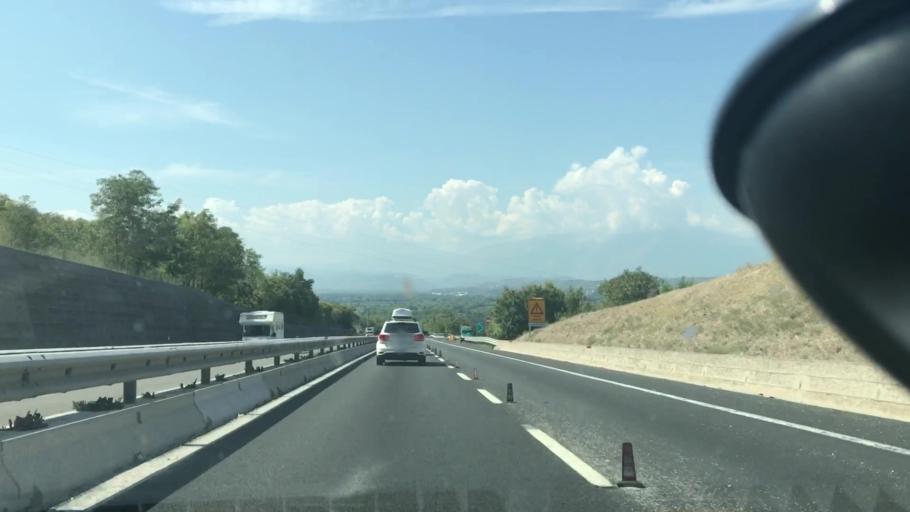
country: IT
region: Abruzzo
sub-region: Provincia di Chieti
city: Torino di Sangro
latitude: 42.2027
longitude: 14.5195
